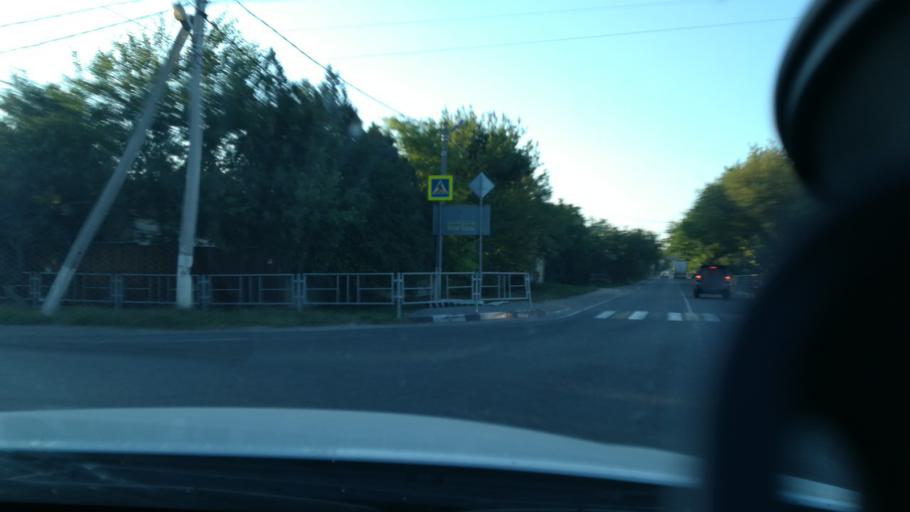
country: RU
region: Krasnodarskiy
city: Gostagayevskaya
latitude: 45.0256
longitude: 37.5032
